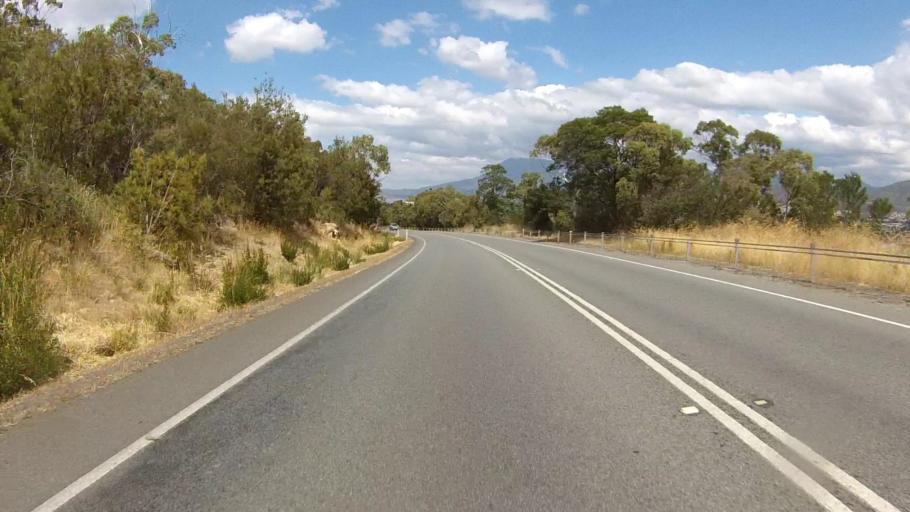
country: AU
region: Tasmania
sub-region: Brighton
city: Old Beach
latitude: -42.7722
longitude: 147.2687
